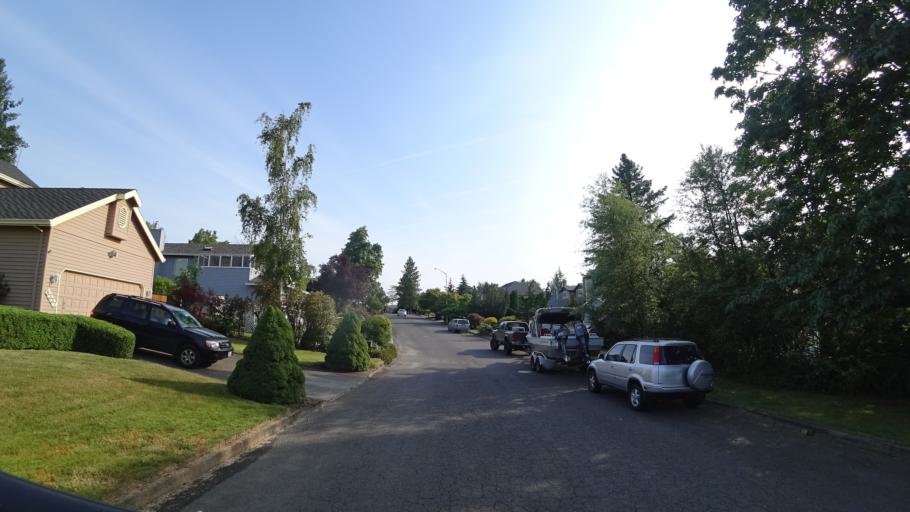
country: US
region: Oregon
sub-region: Clackamas County
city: Happy Valley
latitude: 45.4625
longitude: -122.5153
